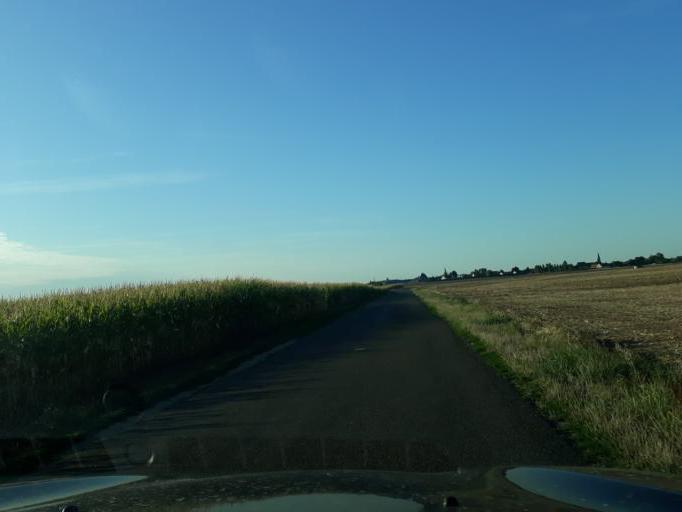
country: FR
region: Centre
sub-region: Departement du Loiret
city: Epieds-en-Beauce
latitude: 47.9386
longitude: 1.5795
